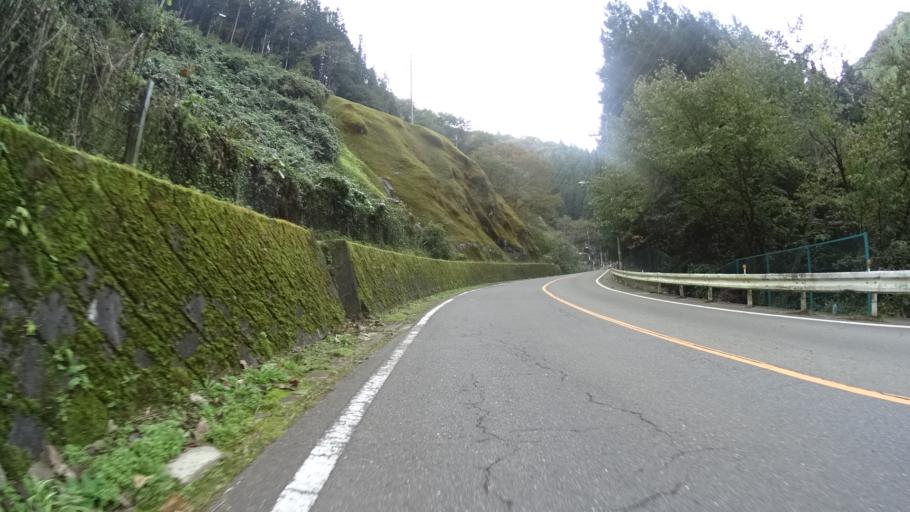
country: JP
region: Yamanashi
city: Uenohara
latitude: 35.6984
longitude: 139.1006
